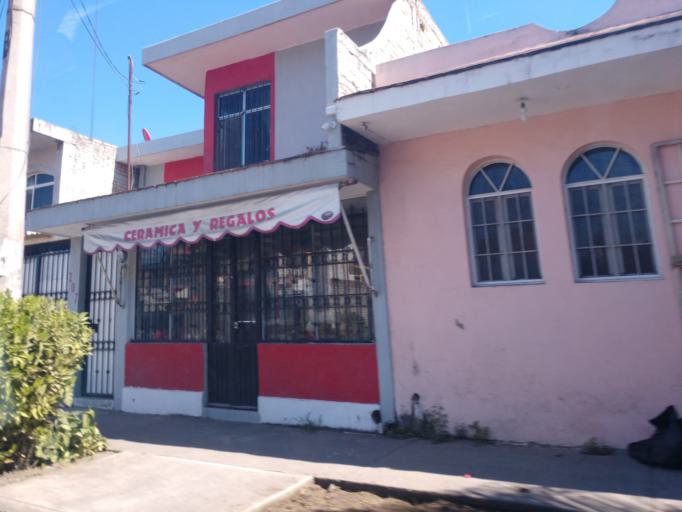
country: MX
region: Nayarit
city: Xalisco
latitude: 21.4720
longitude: -104.8703
